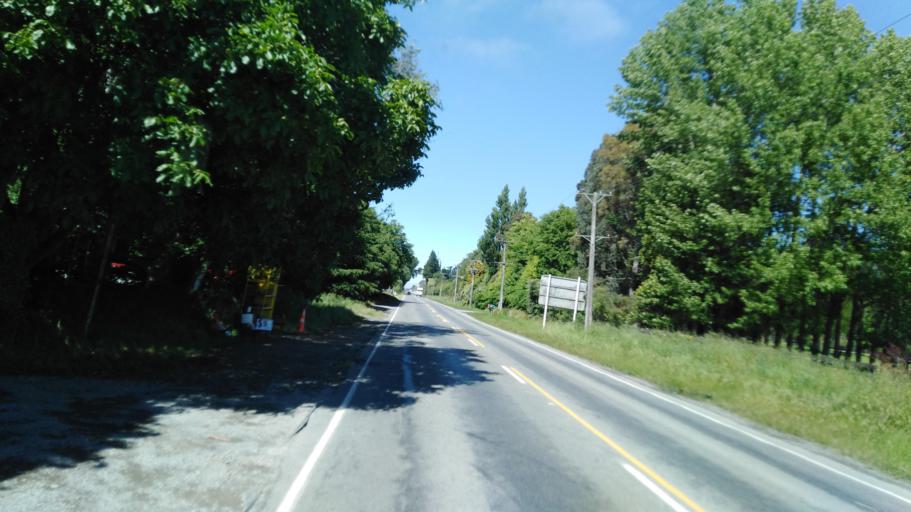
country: NZ
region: Canterbury
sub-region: Selwyn District
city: Prebbleton
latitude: -43.5206
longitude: 172.5042
